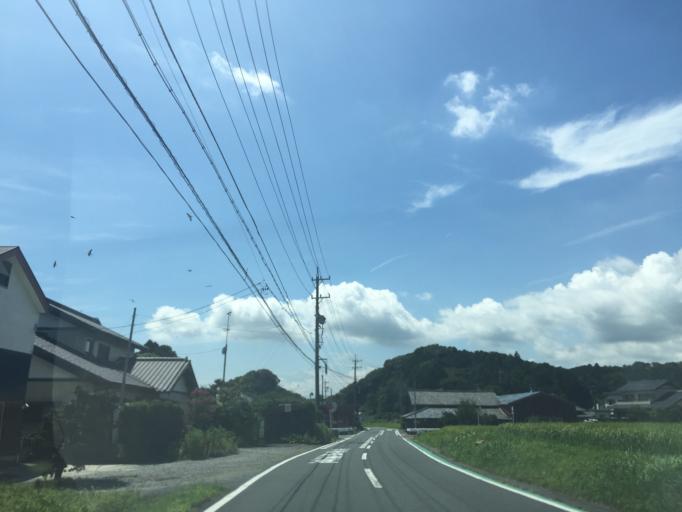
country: JP
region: Shizuoka
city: Kanaya
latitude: 34.7887
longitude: 138.0765
